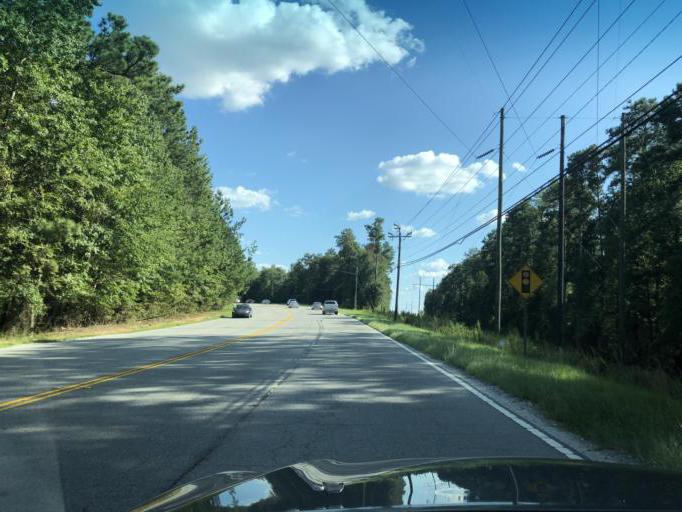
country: US
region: Georgia
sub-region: Muscogee County
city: Columbus
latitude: 32.5127
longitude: -84.8940
